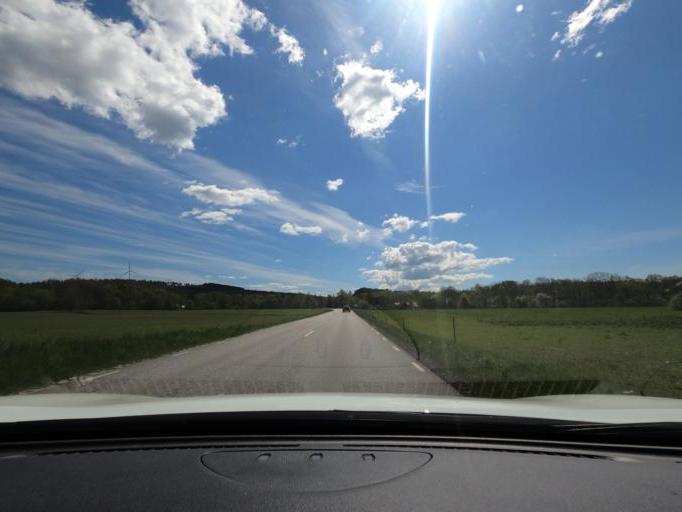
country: SE
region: Halland
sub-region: Kungsbacka Kommun
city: Fjaeras kyrkby
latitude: 57.4198
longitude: 12.2041
